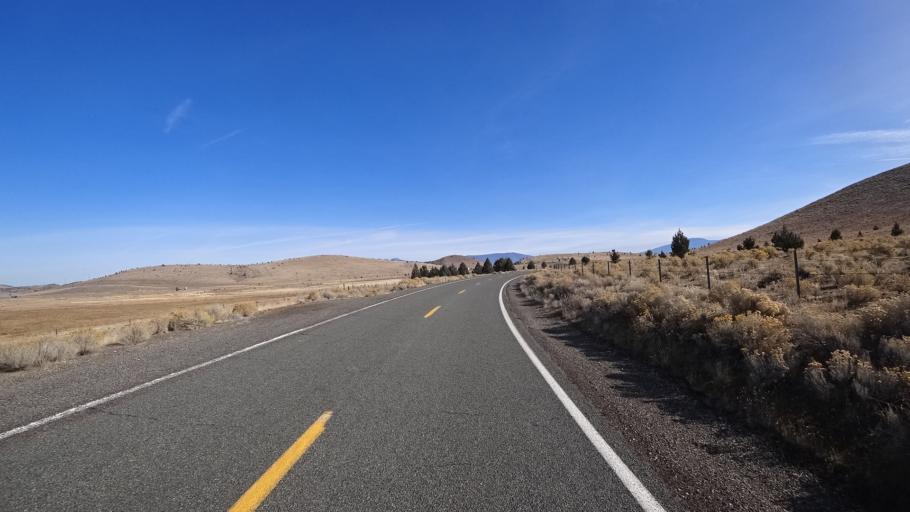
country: US
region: California
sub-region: Siskiyou County
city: Weed
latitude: 41.5508
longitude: -122.4909
